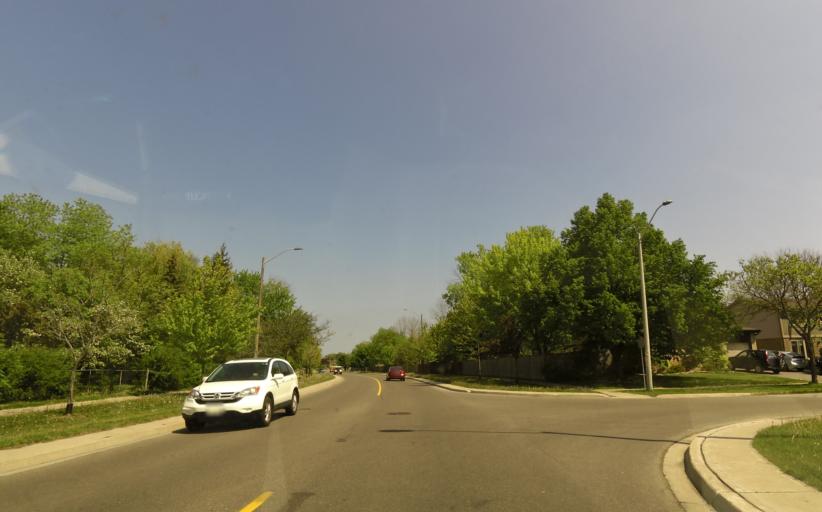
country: CA
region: Ontario
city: Mississauga
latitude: 43.5919
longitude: -79.6185
